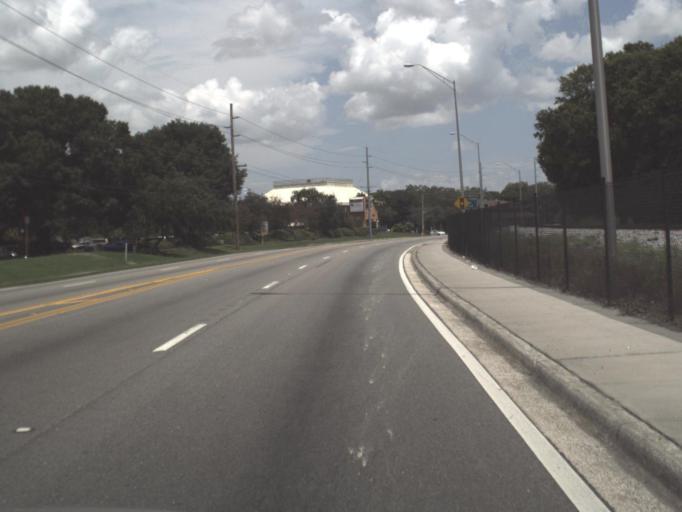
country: US
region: Florida
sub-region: Hillsborough County
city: Carrollwood
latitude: 28.0358
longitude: -82.4910
